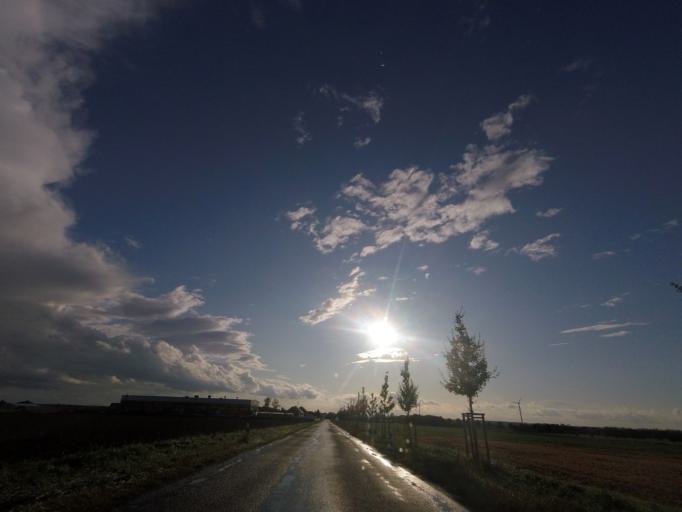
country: DE
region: Saxony-Anhalt
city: Kropstadt
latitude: 52.0055
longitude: 12.7896
